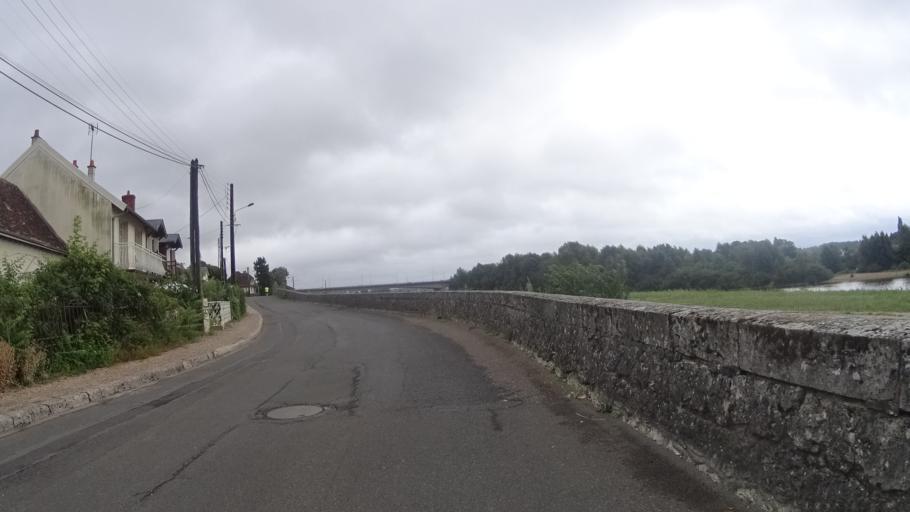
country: FR
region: Centre
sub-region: Departement du Loir-et-Cher
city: Blois
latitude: 47.5926
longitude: 1.3487
